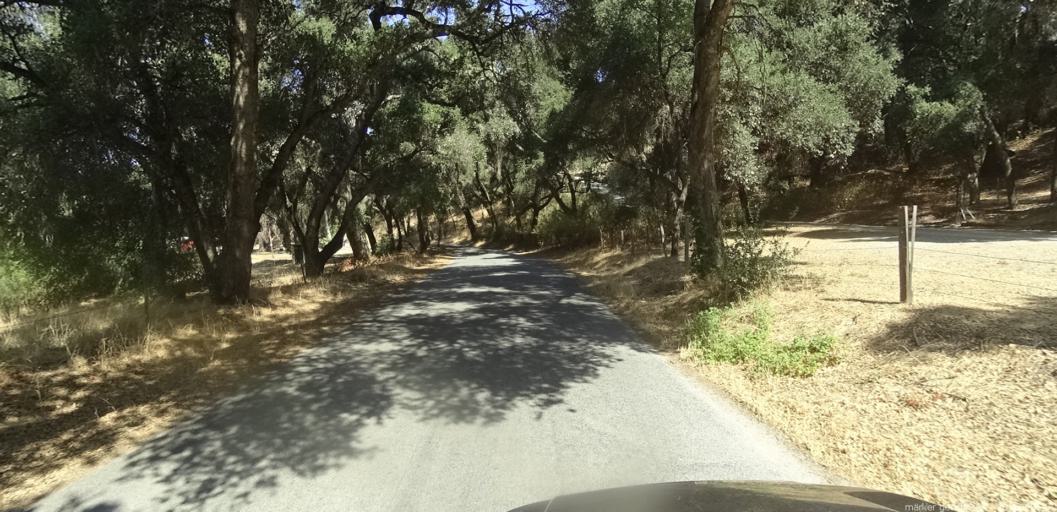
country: US
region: California
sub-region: Monterey County
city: Carmel Valley Village
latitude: 36.3986
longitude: -121.6513
